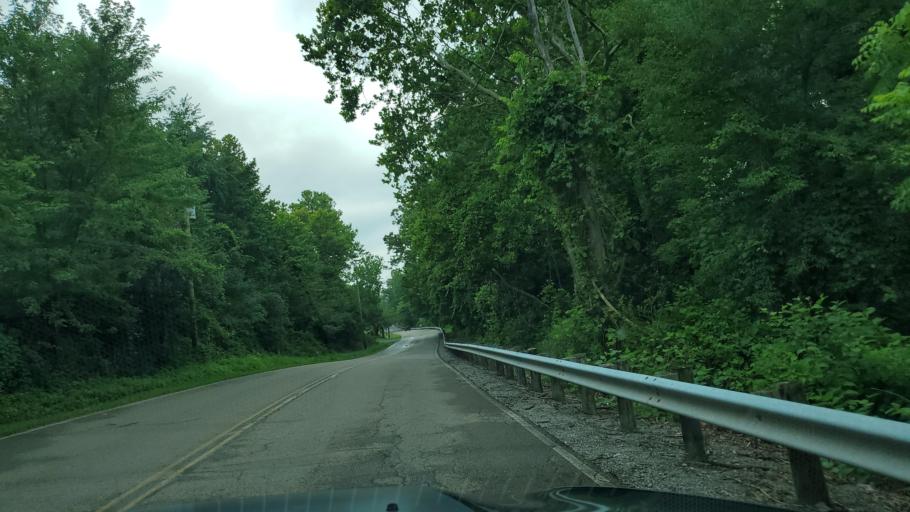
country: US
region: Ohio
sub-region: Mahoning County
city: Lowellville
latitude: 41.0415
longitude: -80.5509
